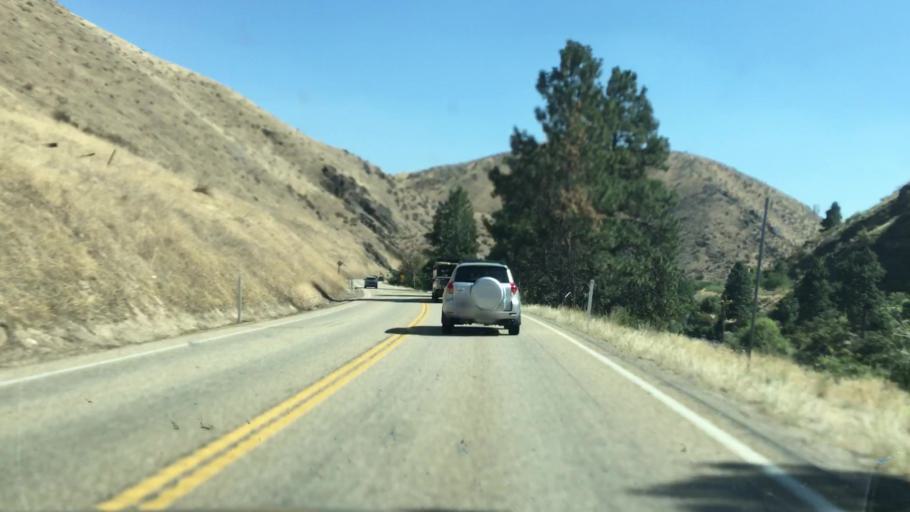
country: US
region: Idaho
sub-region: Ada County
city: Eagle
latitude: 43.9542
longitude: -116.1946
